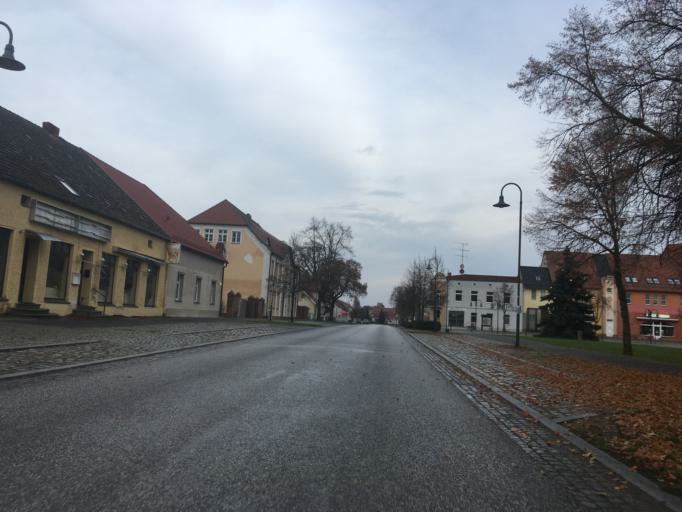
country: DE
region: Brandenburg
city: Letschin
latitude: 52.6445
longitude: 14.3601
